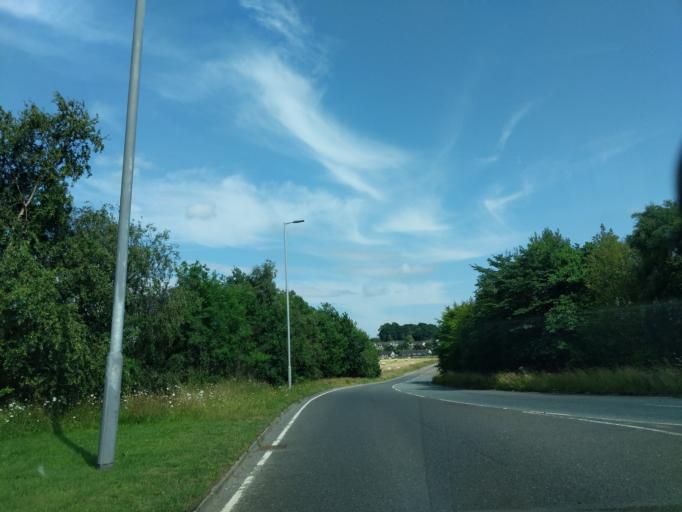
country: GB
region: Scotland
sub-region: Moray
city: Lhanbryd
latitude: 57.6358
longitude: -3.2329
